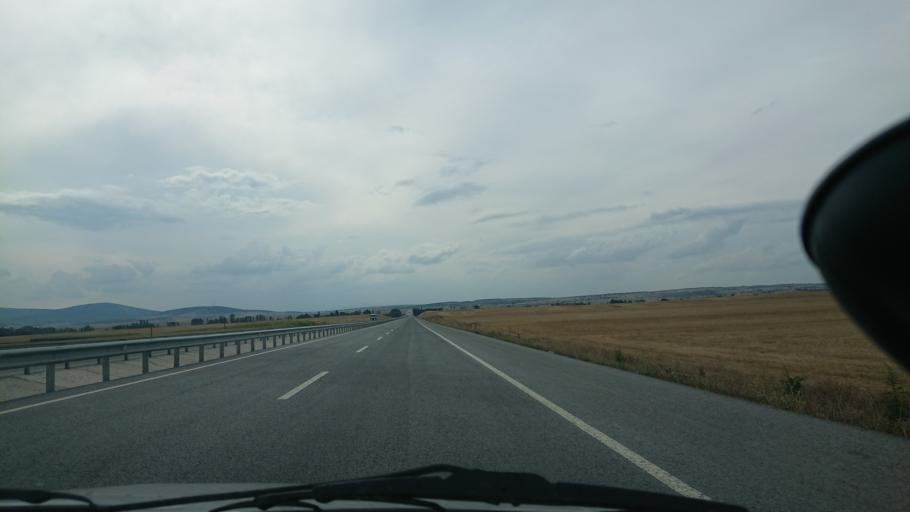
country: TR
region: Kuetahya
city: Aslanapa
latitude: 39.2547
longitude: 29.8607
